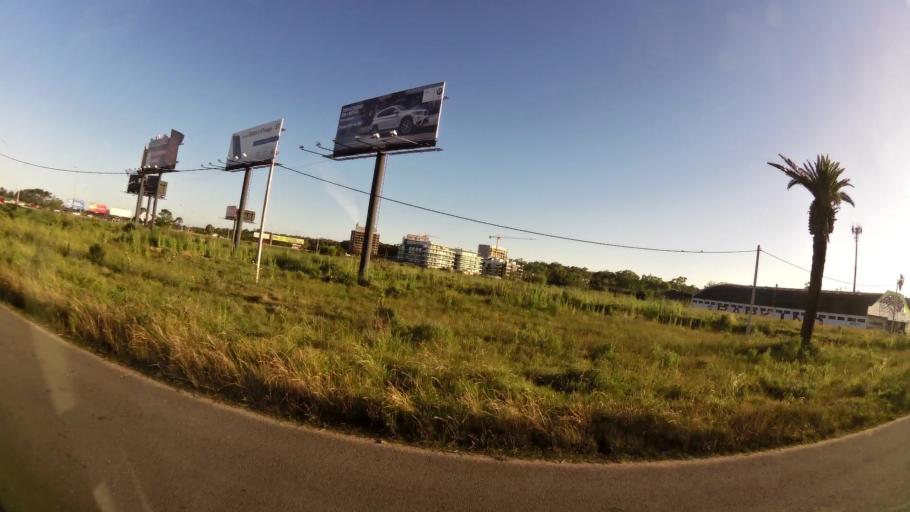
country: UY
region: Canelones
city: Paso de Carrasco
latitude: -34.8462
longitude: -56.0254
